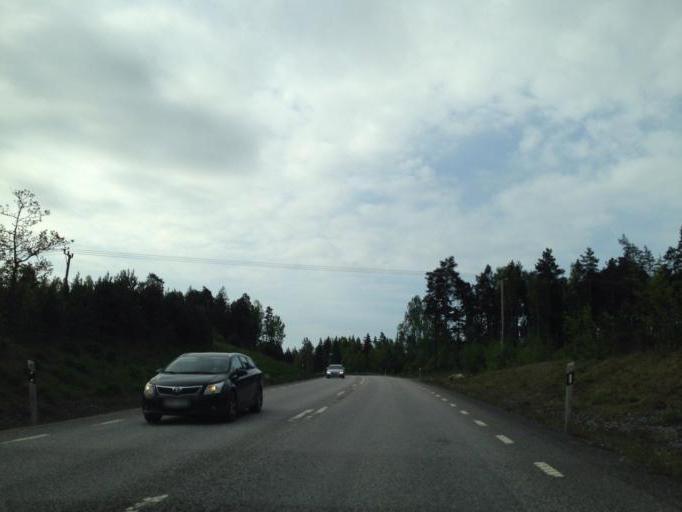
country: SE
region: Soedermanland
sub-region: Eskilstuna Kommun
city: Skogstorp
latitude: 59.3379
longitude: 16.4601
